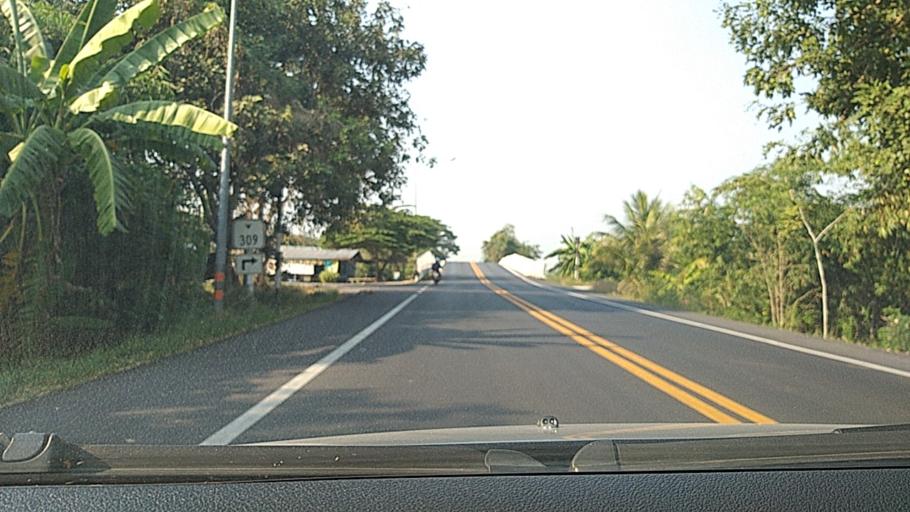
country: TH
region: Sing Buri
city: Phrom Buri
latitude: 14.7569
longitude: 100.4354
